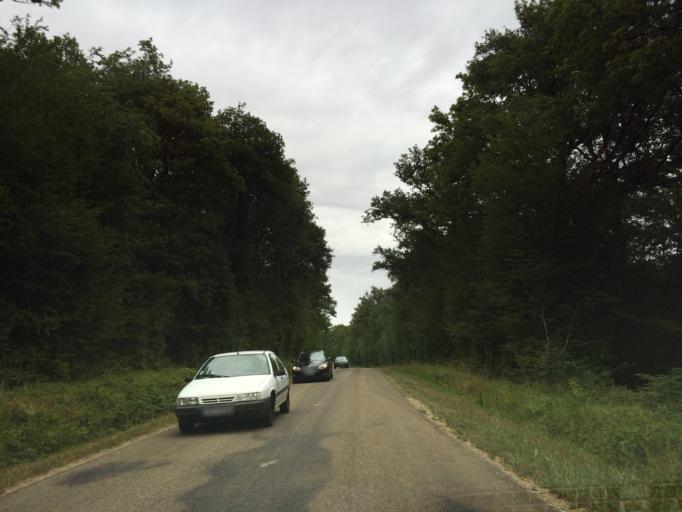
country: FR
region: Bourgogne
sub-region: Departement de l'Yonne
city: Aillant-sur-Tholon
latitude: 47.8644
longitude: 3.2952
